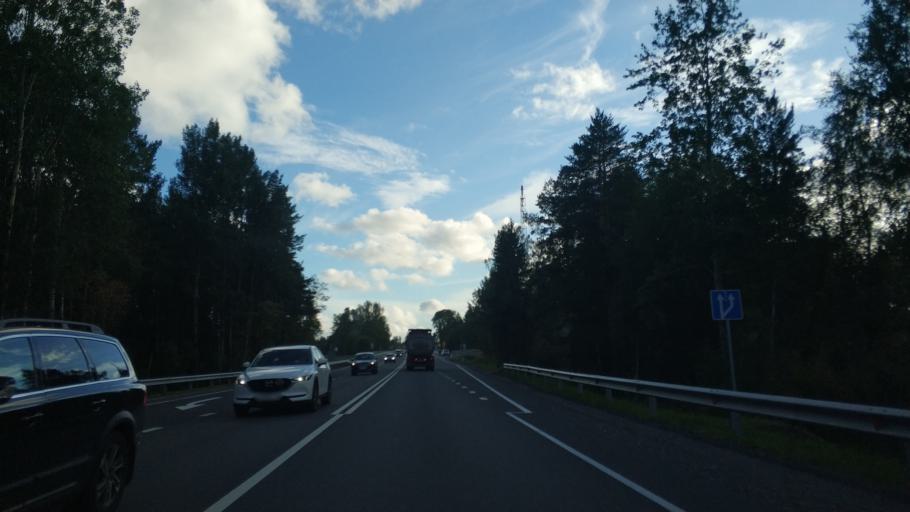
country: RU
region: Leningrad
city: Priozersk
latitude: 60.8542
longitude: 30.1517
